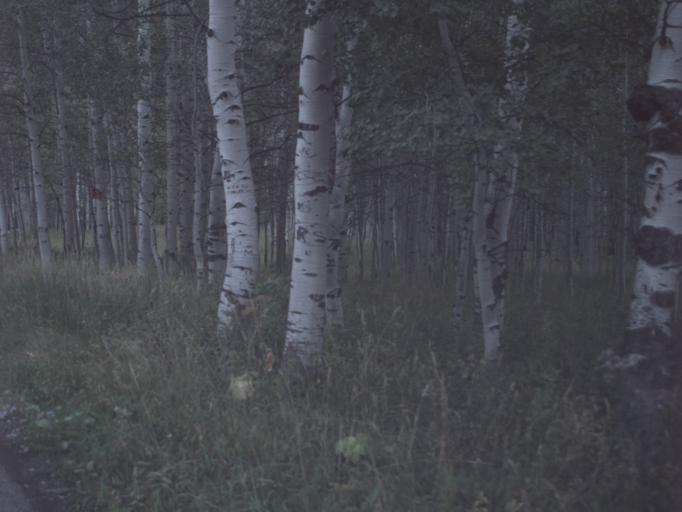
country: US
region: Utah
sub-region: Utah County
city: Lindon
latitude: 40.4185
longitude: -111.6027
